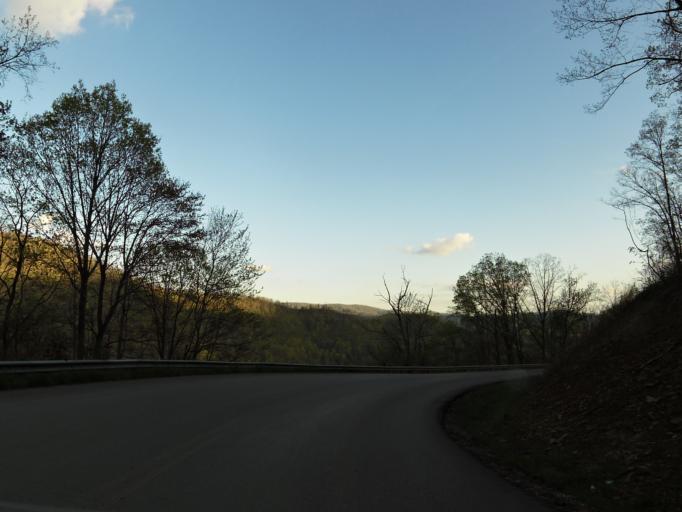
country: US
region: Kentucky
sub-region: Bell County
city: Middlesboro
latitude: 36.6218
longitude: -83.8692
